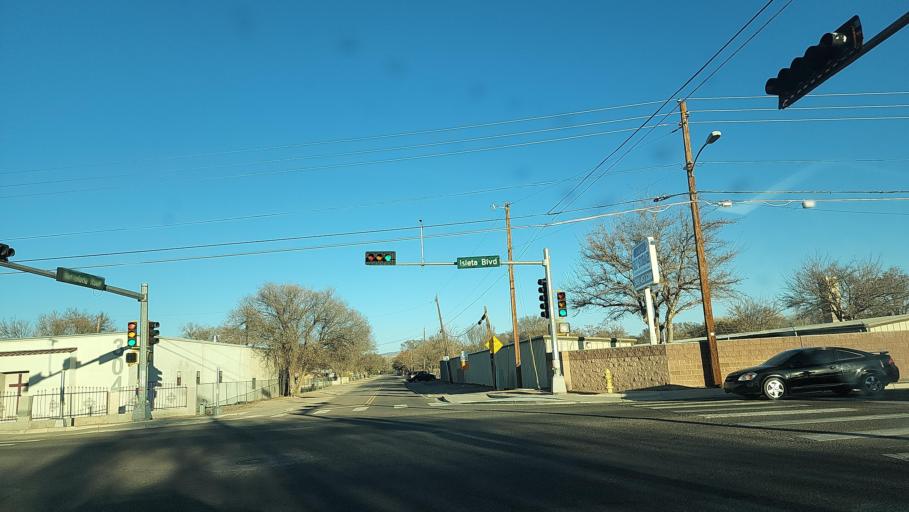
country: US
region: New Mexico
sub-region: Bernalillo County
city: South Valley
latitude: 35.0307
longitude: -106.6798
